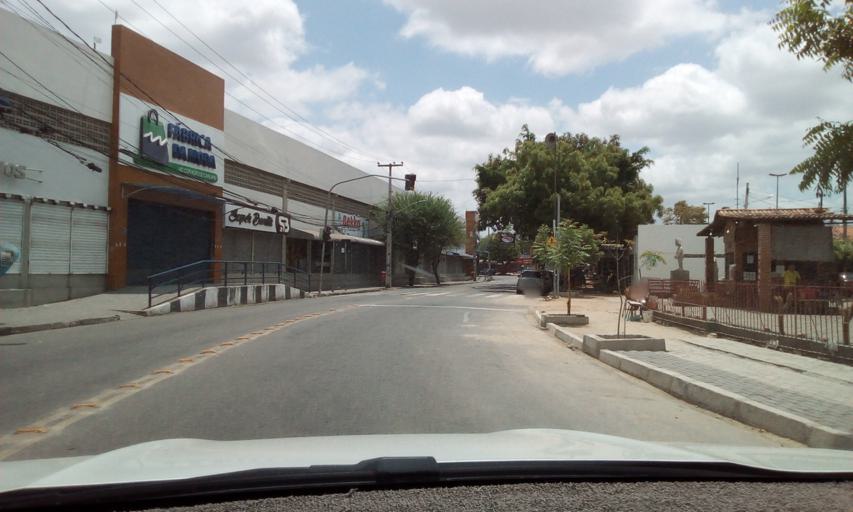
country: BR
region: Pernambuco
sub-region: Caruaru
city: Caruaru
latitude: -8.2893
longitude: -35.9738
